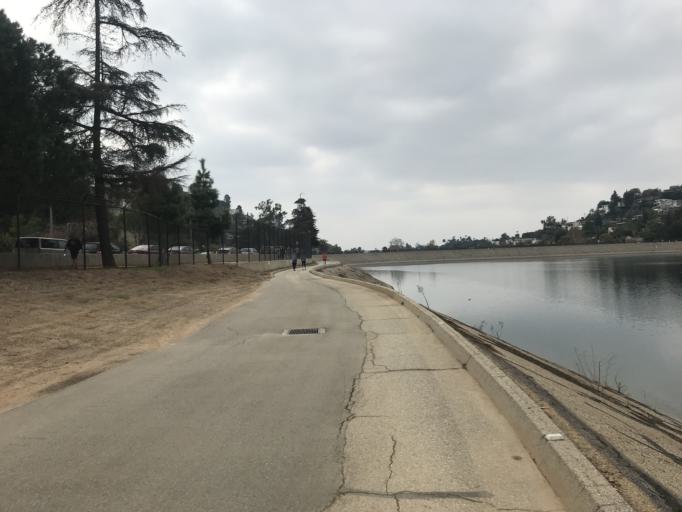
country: US
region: California
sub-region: Los Angeles County
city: Silver Lake
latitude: 34.0948
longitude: -118.2630
